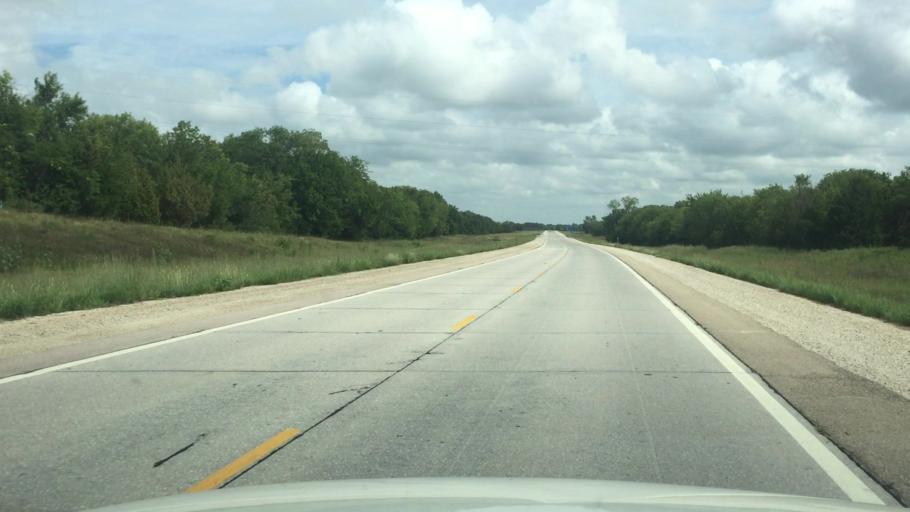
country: US
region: Kansas
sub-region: Allen County
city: Iola
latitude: 37.8998
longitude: -95.3826
